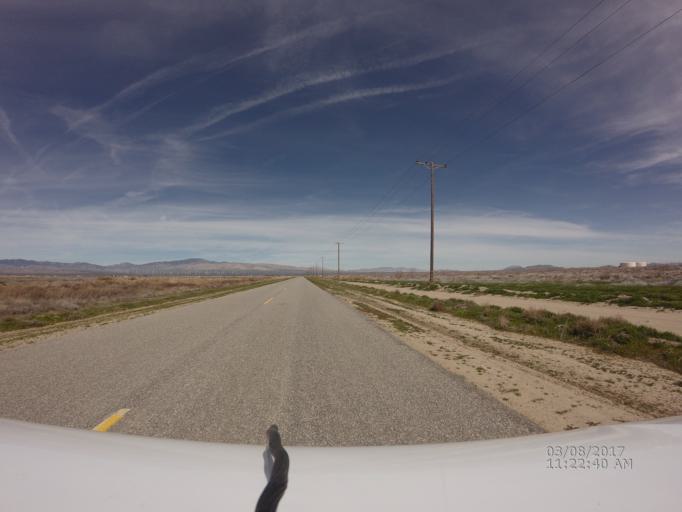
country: US
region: California
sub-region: Los Angeles County
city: Green Valley
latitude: 34.7995
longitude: -118.3790
